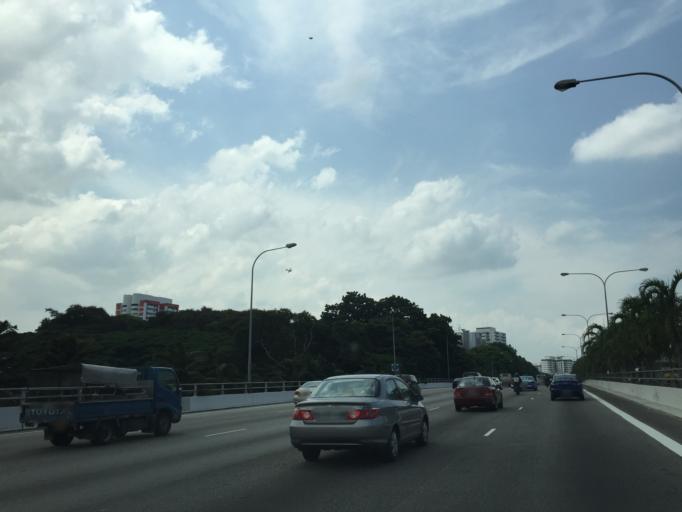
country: SG
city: Singapore
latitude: 1.3203
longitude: 103.8800
